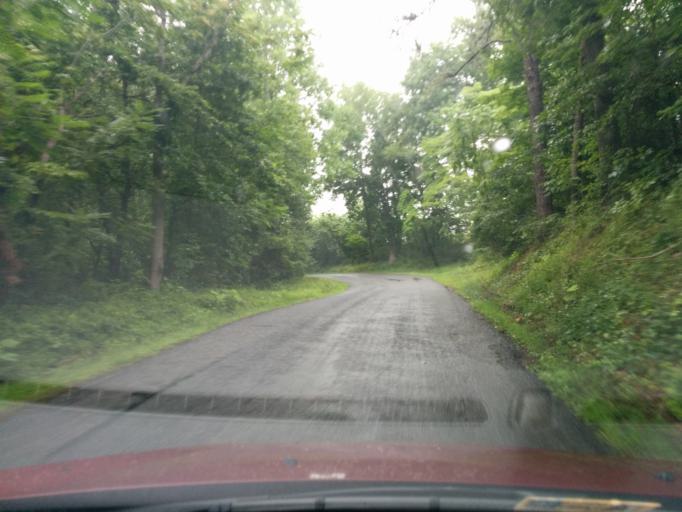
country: US
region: Virginia
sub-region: Rockbridge County
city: East Lexington
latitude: 37.8682
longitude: -79.4243
